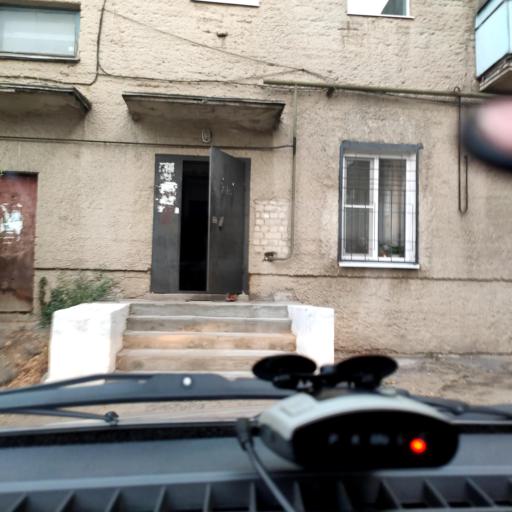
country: RU
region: Voronezj
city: Voronezh
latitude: 51.6640
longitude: 39.1337
